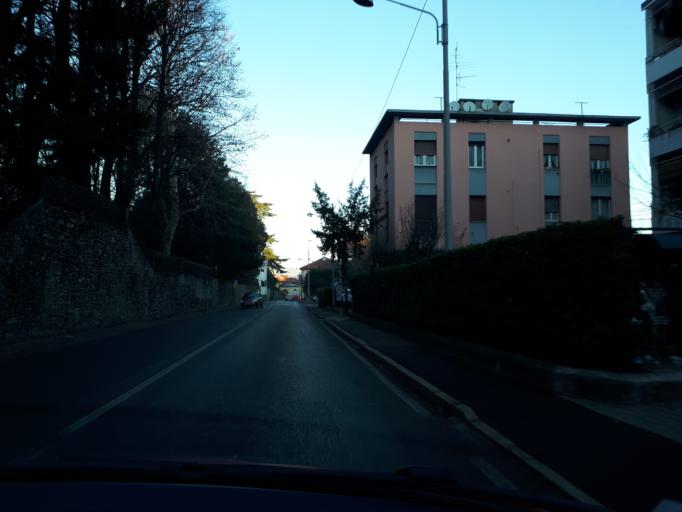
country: IT
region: Lombardy
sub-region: Provincia di Como
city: Fino Mornasco
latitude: 45.7406
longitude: 9.0518
